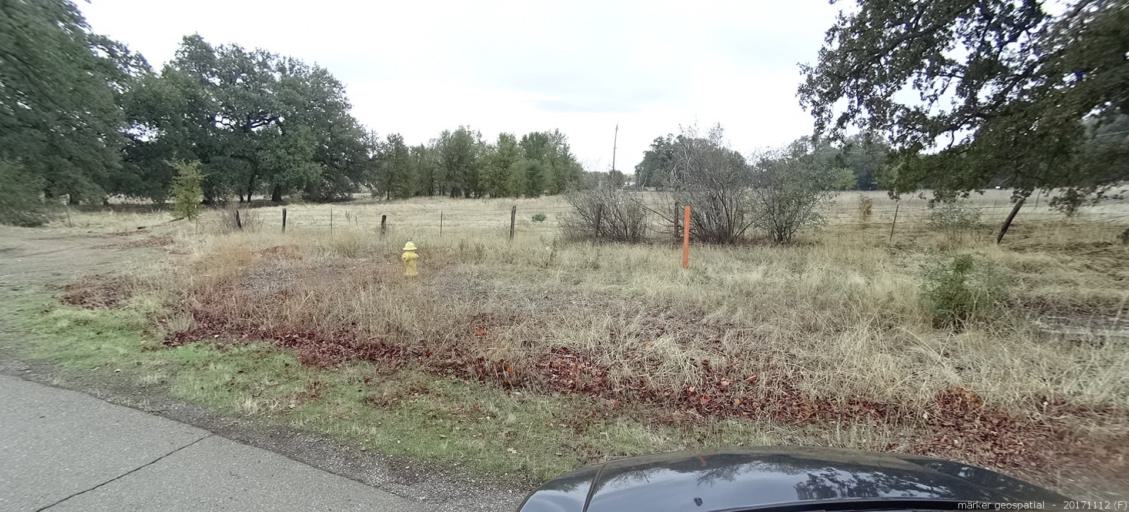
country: US
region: California
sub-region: Shasta County
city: Palo Cedro
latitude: 40.5566
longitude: -122.2427
